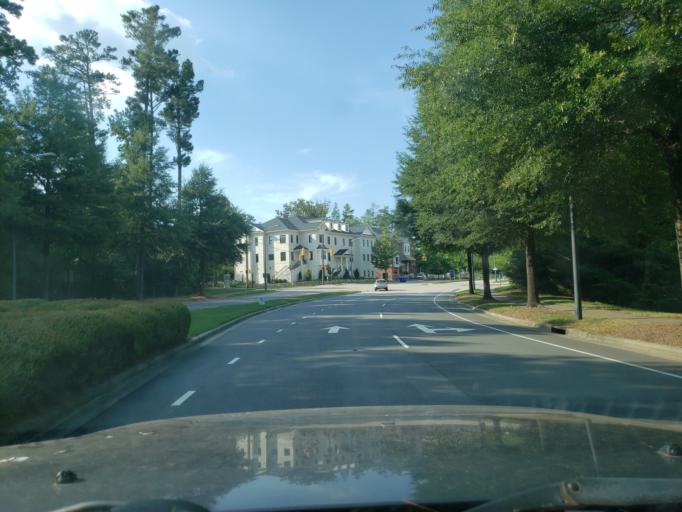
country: US
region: North Carolina
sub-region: Orange County
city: Chapel Hill
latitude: 35.9066
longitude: -79.0092
